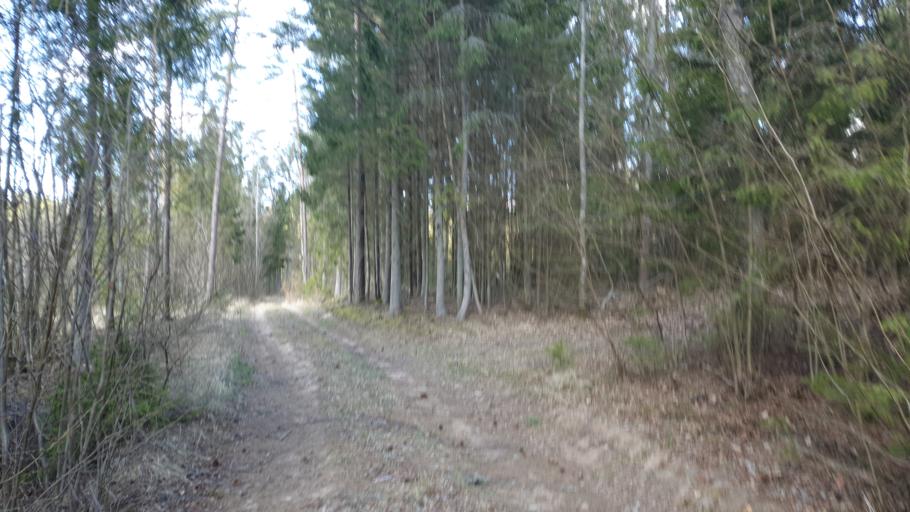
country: LT
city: Aukstadvaris
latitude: 54.4946
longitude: 24.6510
